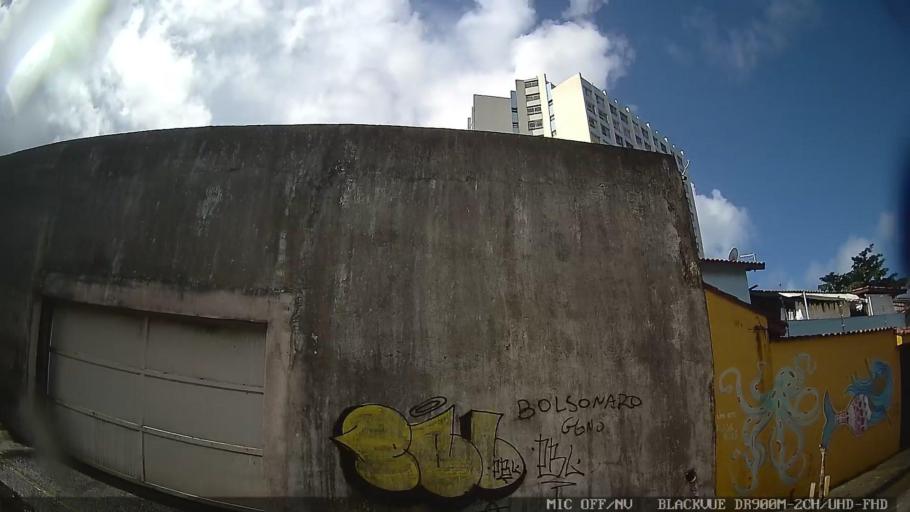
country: BR
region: Sao Paulo
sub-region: Itanhaem
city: Itanhaem
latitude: -24.1910
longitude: -46.8023
